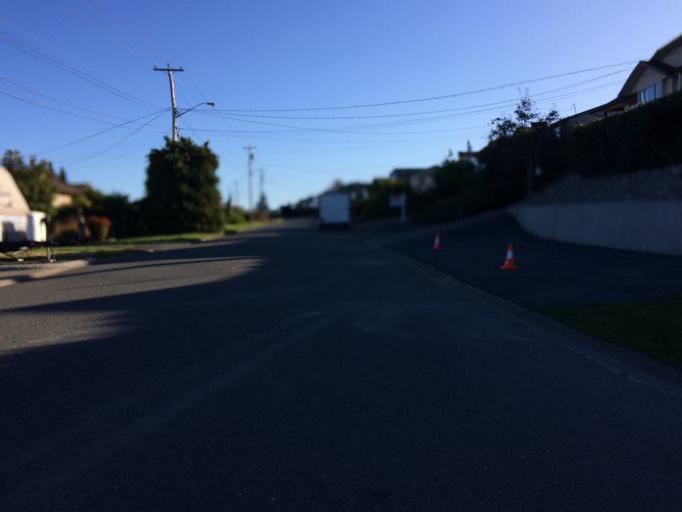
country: CA
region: British Columbia
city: Campbell River
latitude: 49.9973
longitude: -125.2338
